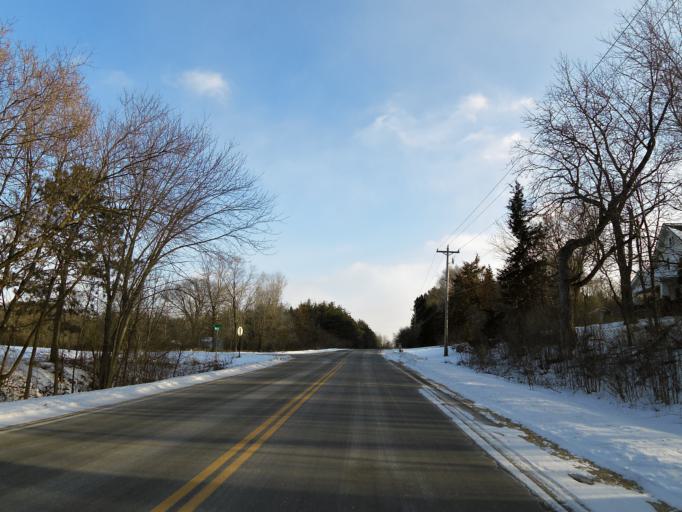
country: US
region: Minnesota
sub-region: Washington County
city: Lake Elmo
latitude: 44.9748
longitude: -92.8623
